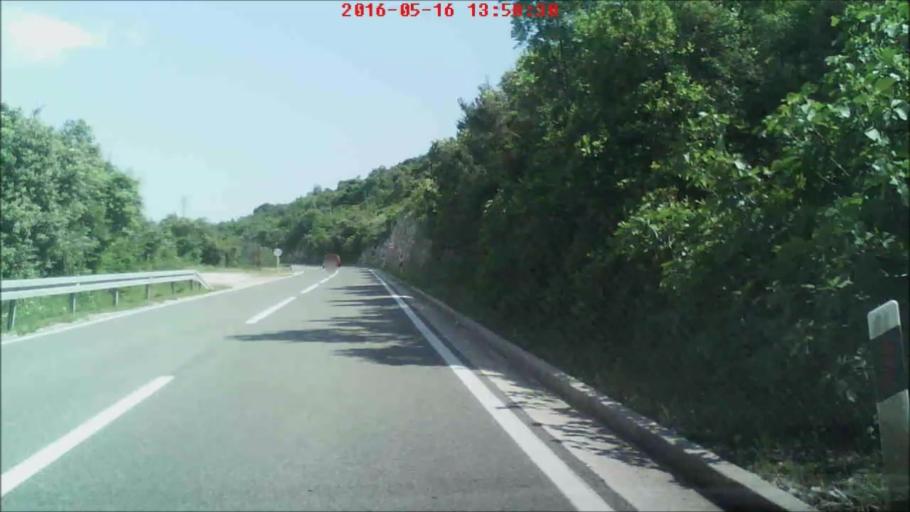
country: HR
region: Dubrovacko-Neretvanska
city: Ston
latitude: 42.8390
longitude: 17.7171
